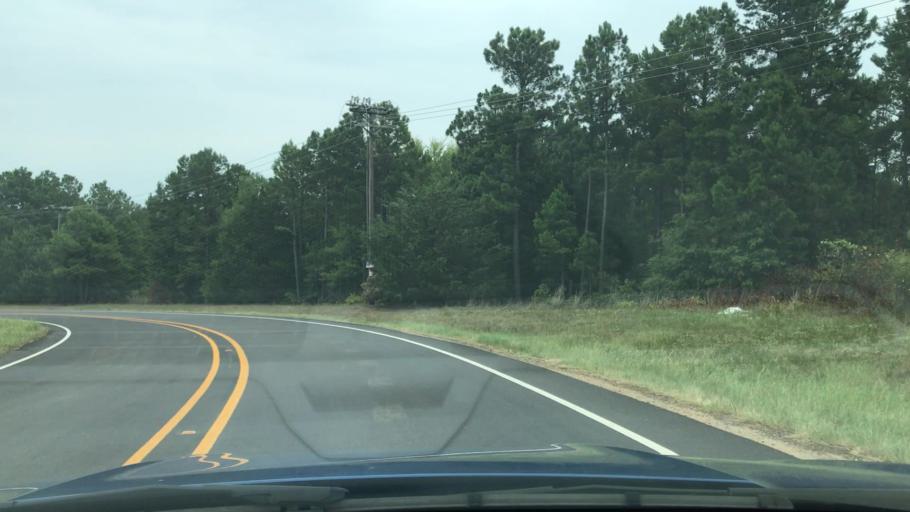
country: US
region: Texas
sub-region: Smith County
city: Hideaway
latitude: 32.4683
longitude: -95.4542
